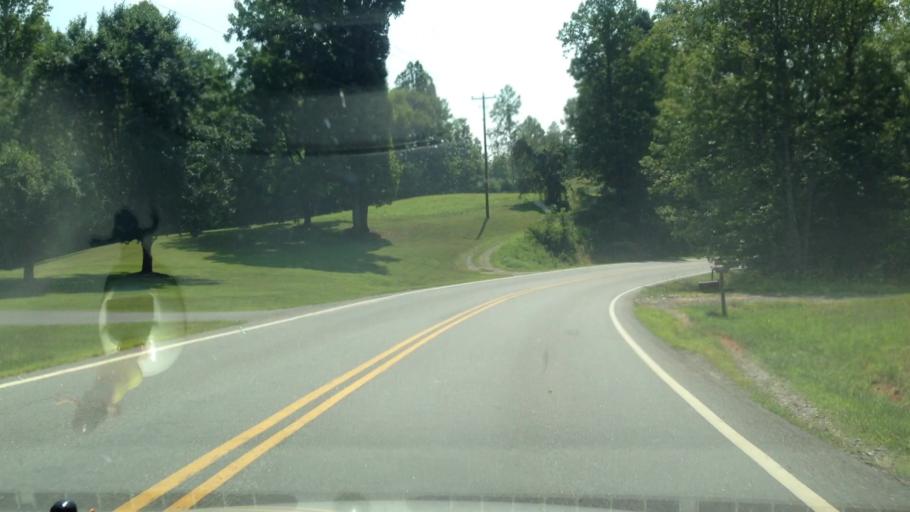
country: US
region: Virginia
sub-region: Patrick County
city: Stuart
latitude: 36.5861
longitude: -80.3910
